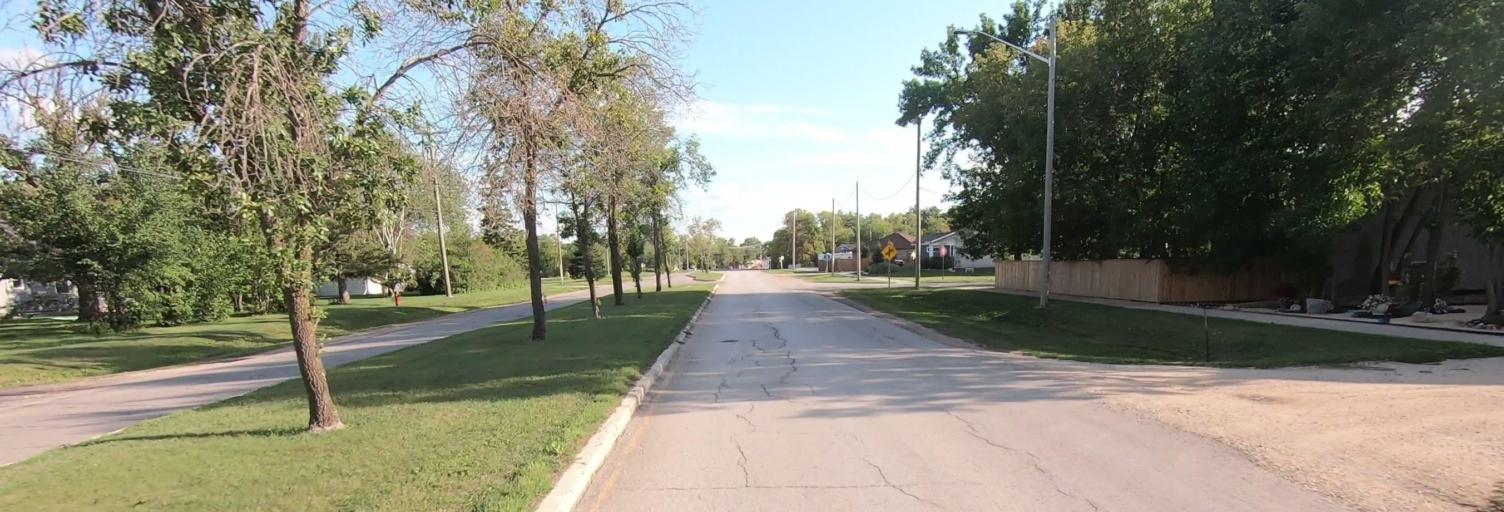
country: CA
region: Manitoba
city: Selkirk
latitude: 50.1517
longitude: -96.8670
